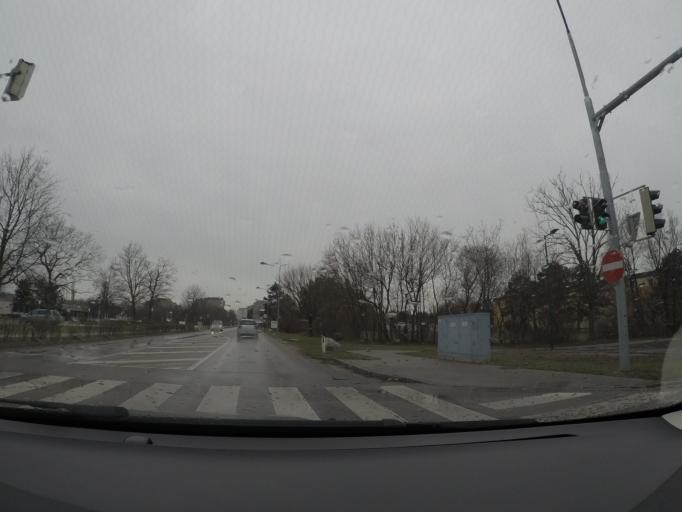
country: AT
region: Lower Austria
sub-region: Politischer Bezirk Modling
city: Wiener Neudorf
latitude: 48.0944
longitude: 16.3104
